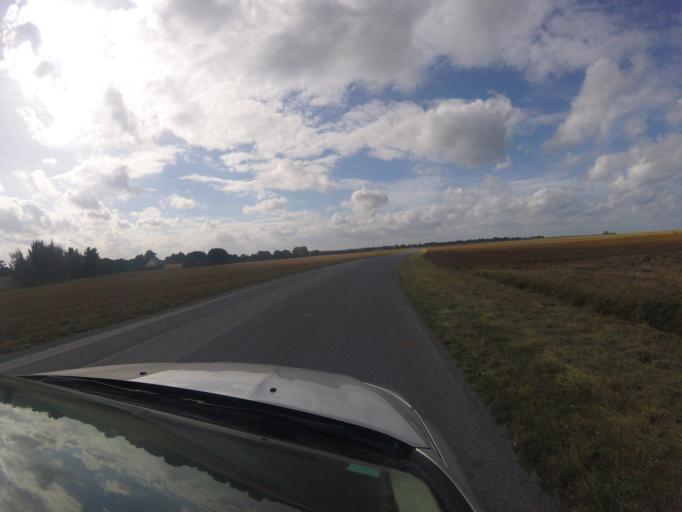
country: FR
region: Lower Normandy
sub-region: Departement du Calvados
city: Saint-Vigor-le-Grand
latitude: 49.3321
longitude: -0.6735
